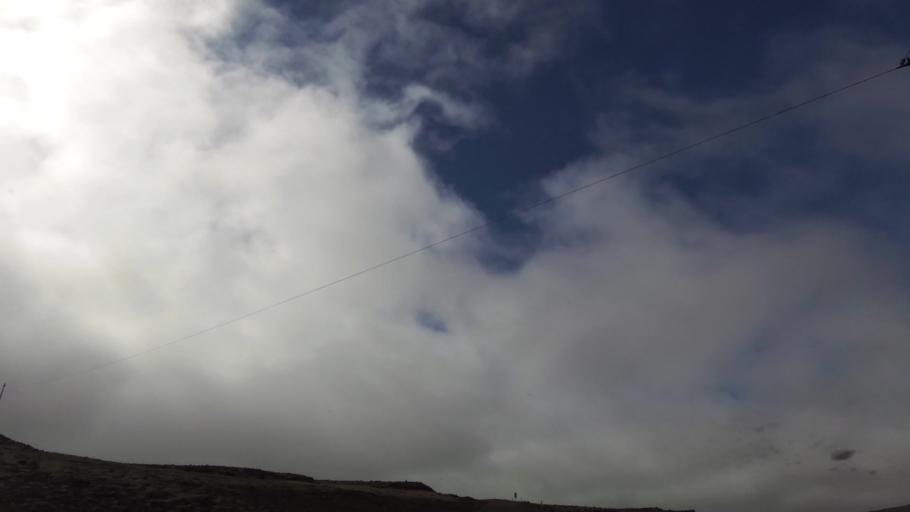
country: IS
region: West
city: Olafsvik
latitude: 65.5433
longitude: -24.3121
